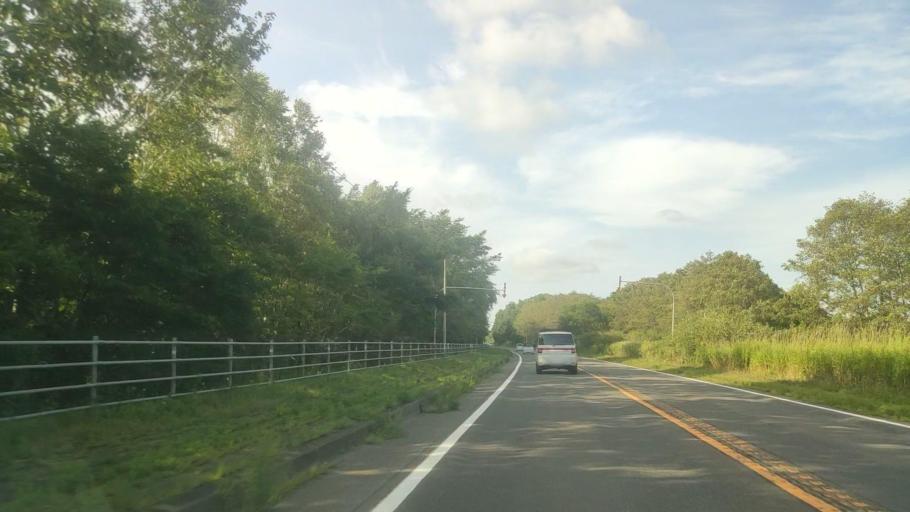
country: JP
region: Hokkaido
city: Chitose
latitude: 42.8618
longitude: 141.8224
